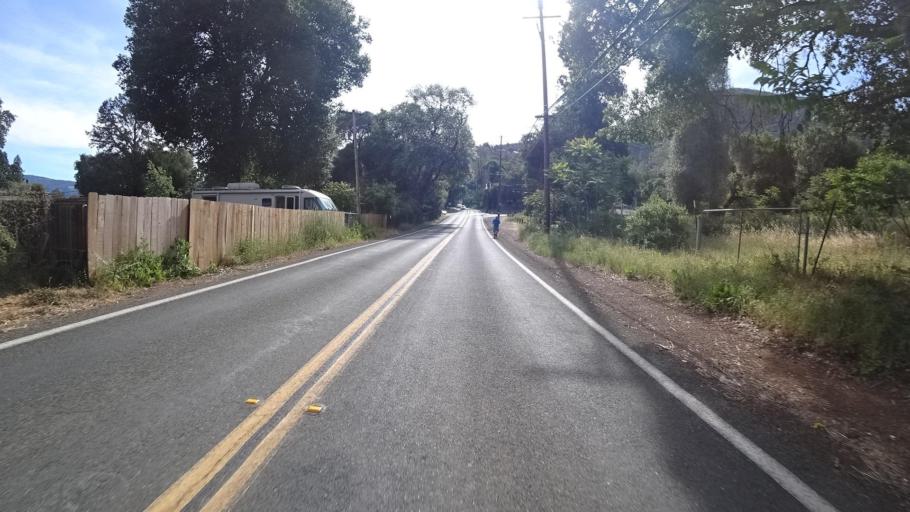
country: US
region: California
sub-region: Lake County
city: Soda Bay
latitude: 39.0012
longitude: -122.7901
